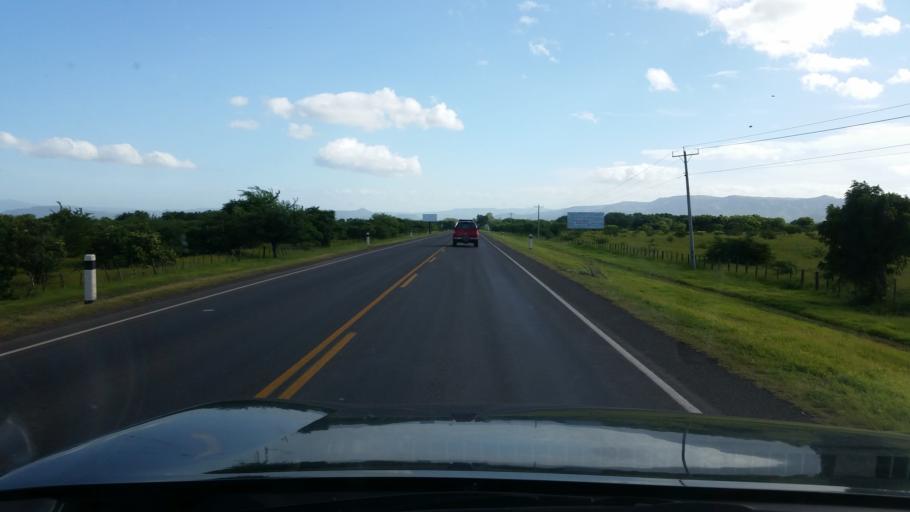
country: NI
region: Managua
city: Tipitapa
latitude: 12.3222
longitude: -86.0531
